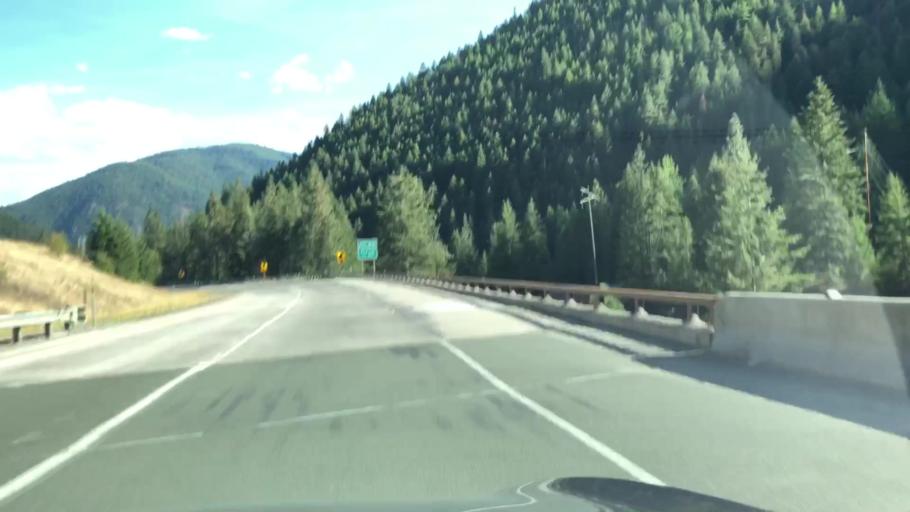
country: US
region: Montana
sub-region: Sanders County
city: Thompson Falls
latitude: 47.3291
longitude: -115.2579
